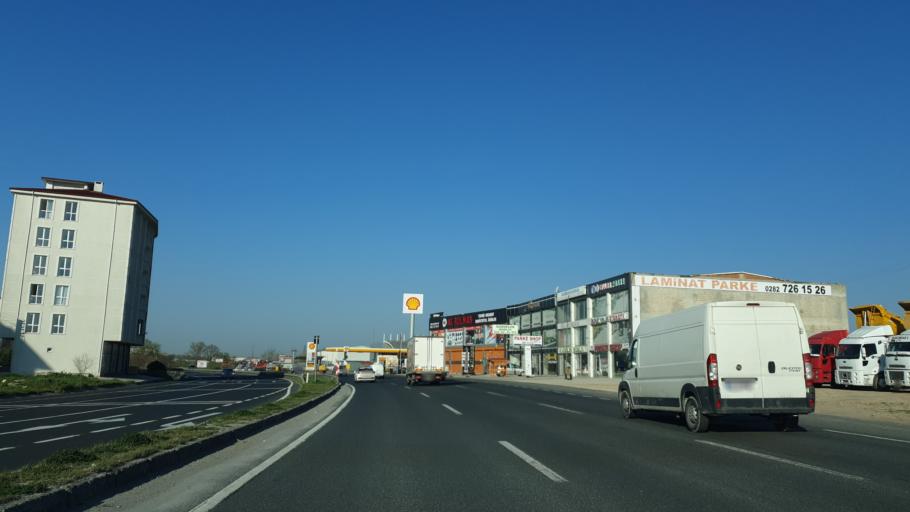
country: TR
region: Tekirdag
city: Cerkezkoey
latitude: 41.2717
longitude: 27.9628
